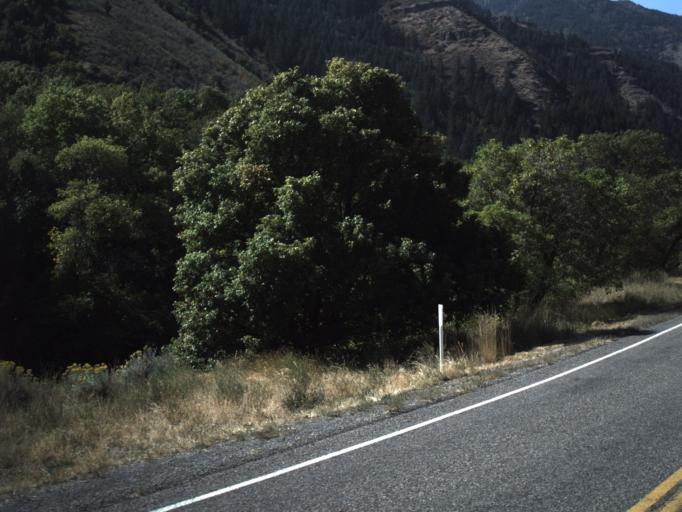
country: US
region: Utah
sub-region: Cache County
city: Millville
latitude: 41.6241
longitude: -111.7364
